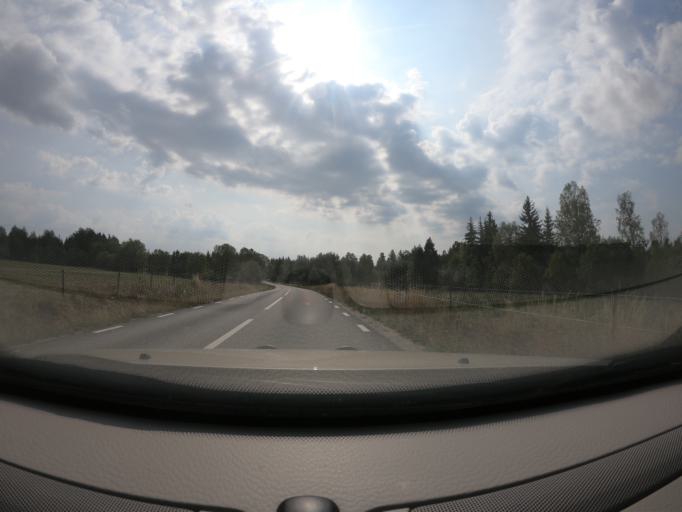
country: SE
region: Kronoberg
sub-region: Vaxjo Kommun
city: Braas
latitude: 57.1393
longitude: 14.9648
